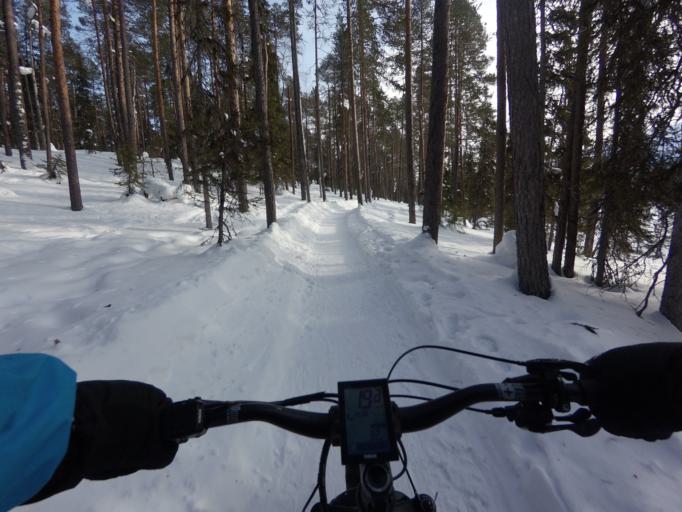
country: FI
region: Lapland
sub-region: Tunturi-Lappi
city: Kolari
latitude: 67.6005
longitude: 24.2444
